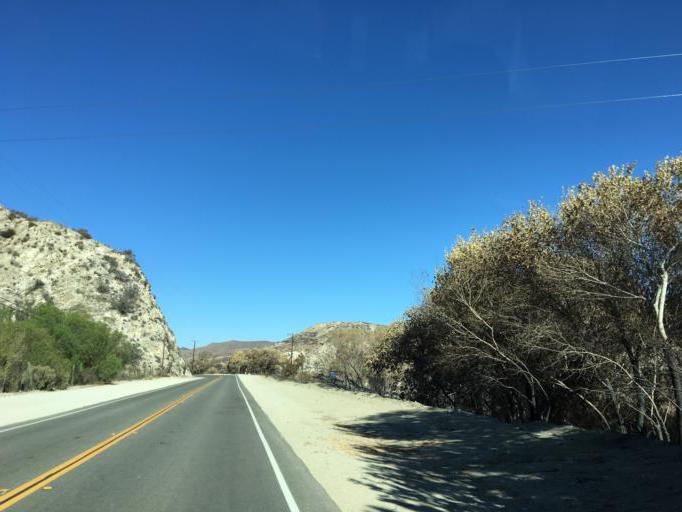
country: US
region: California
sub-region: Los Angeles County
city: Agua Dulce
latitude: 34.4391
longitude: -118.2807
